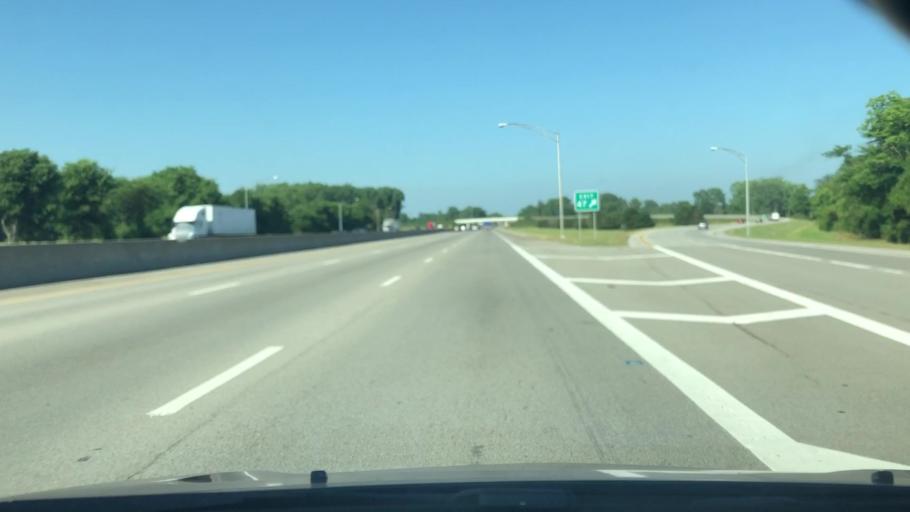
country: US
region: Ohio
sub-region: Clark County
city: Green Meadows
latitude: 39.8816
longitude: -83.9542
